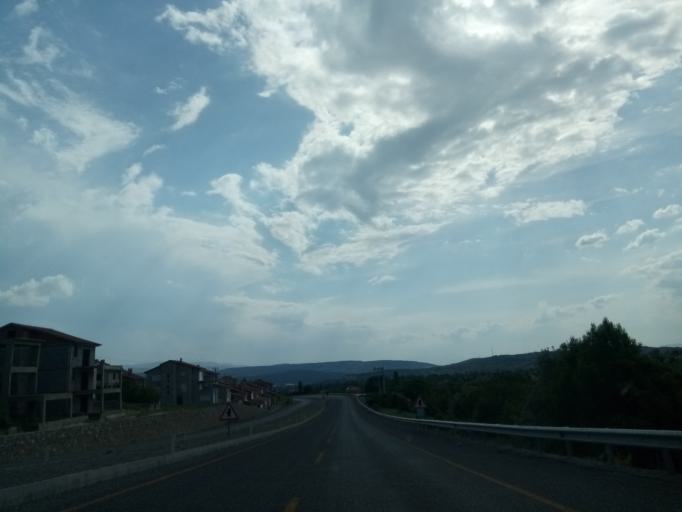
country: TR
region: Isparta
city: Bagkonak
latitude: 38.2157
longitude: 31.2822
